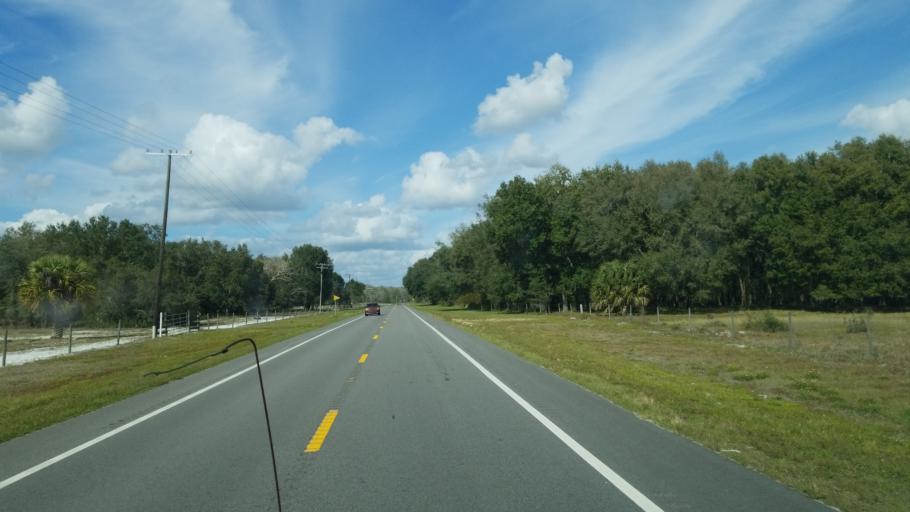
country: US
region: Florida
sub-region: Brevard County
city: June Park
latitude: 27.9368
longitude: -80.9960
